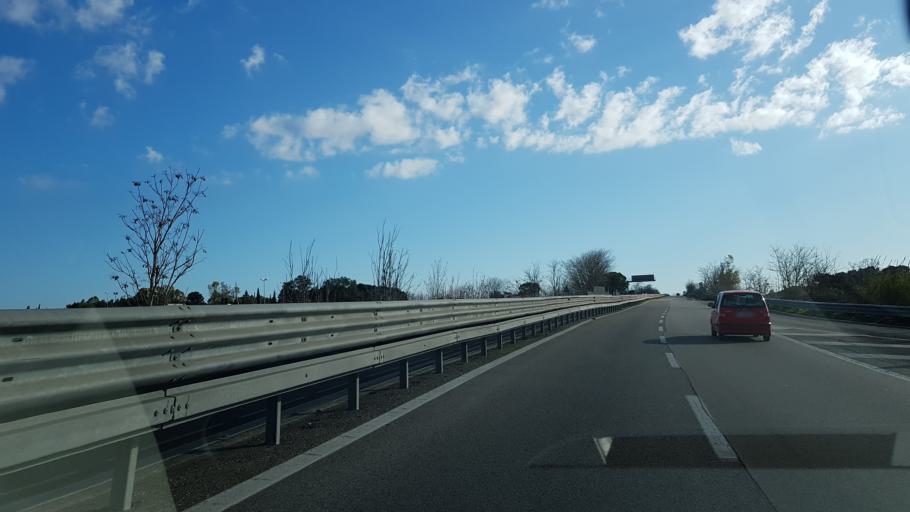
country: IT
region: Apulia
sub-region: Provincia di Lecce
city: Castromediano
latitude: 40.3260
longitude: 18.1628
